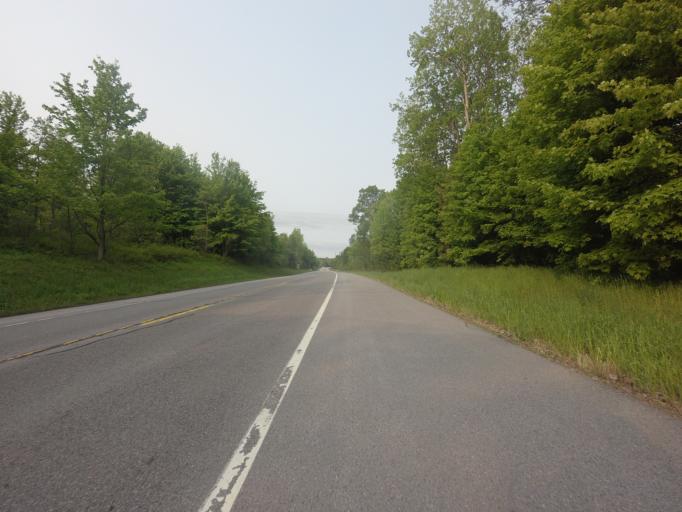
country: US
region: New York
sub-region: Jefferson County
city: Carthage
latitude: 44.0539
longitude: -75.5514
